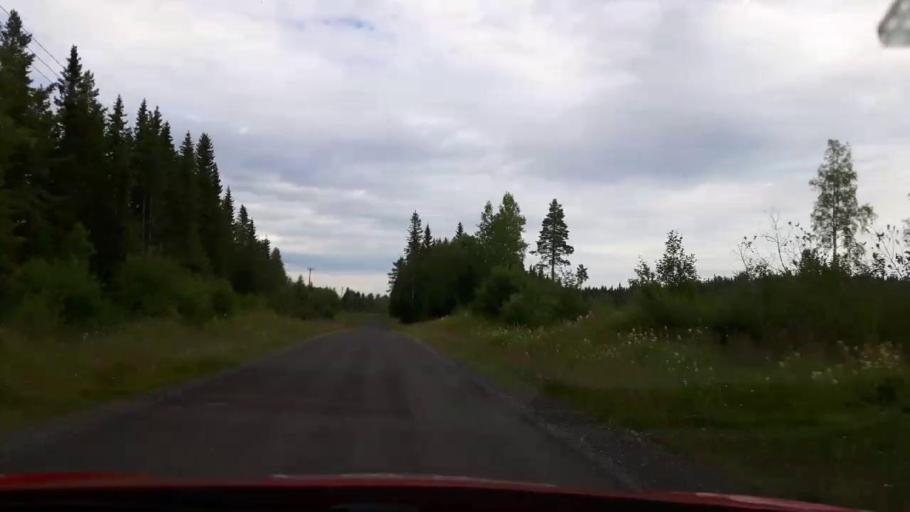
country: SE
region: Jaemtland
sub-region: Stroemsunds Kommun
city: Stroemsund
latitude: 63.5127
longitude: 15.3424
